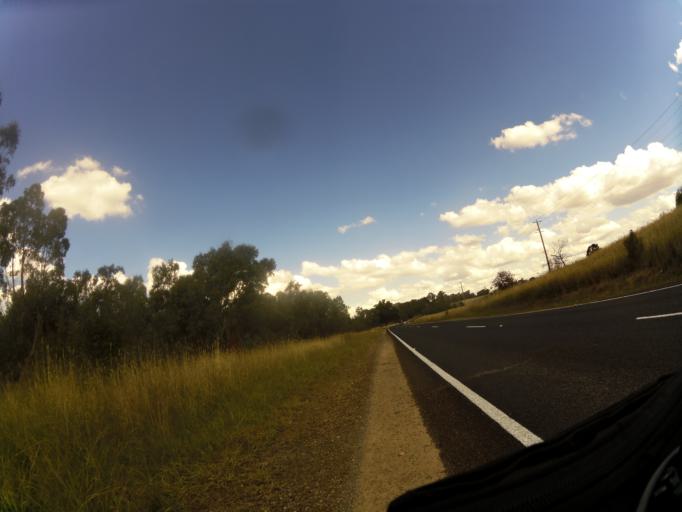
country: AU
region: Victoria
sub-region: Mansfield
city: Mansfield
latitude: -36.9084
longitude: 145.9986
